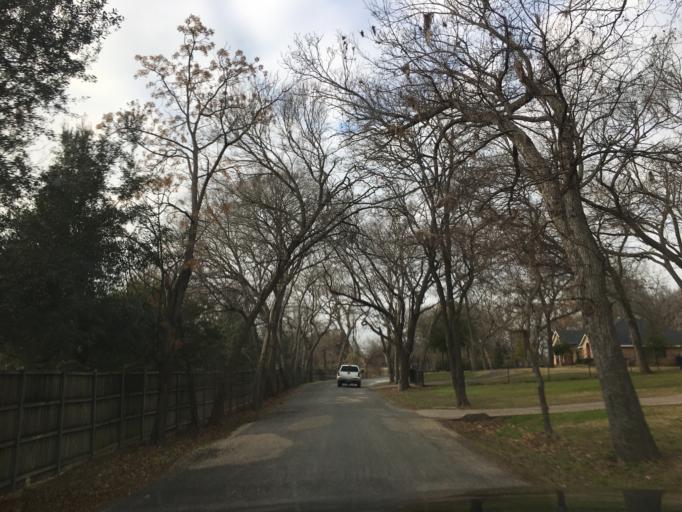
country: US
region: Texas
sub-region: Ellis County
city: Red Oak
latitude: 32.4904
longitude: -96.8006
